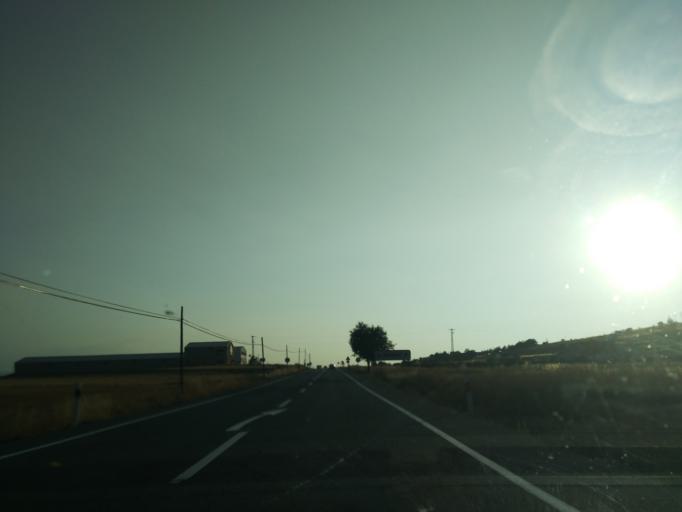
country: ES
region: Castille and Leon
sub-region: Provincia de Avila
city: Martiherrero
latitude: 40.6335
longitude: -4.7627
